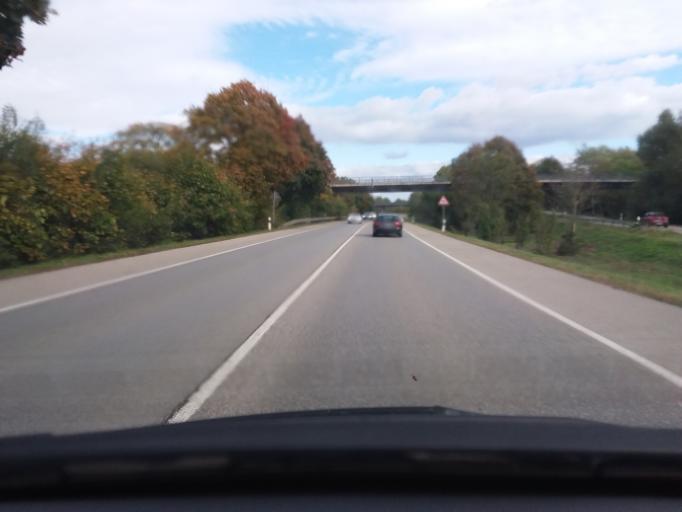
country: DE
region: Bavaria
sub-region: Upper Bavaria
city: Bergkirchen
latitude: 48.2401
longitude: 11.3716
